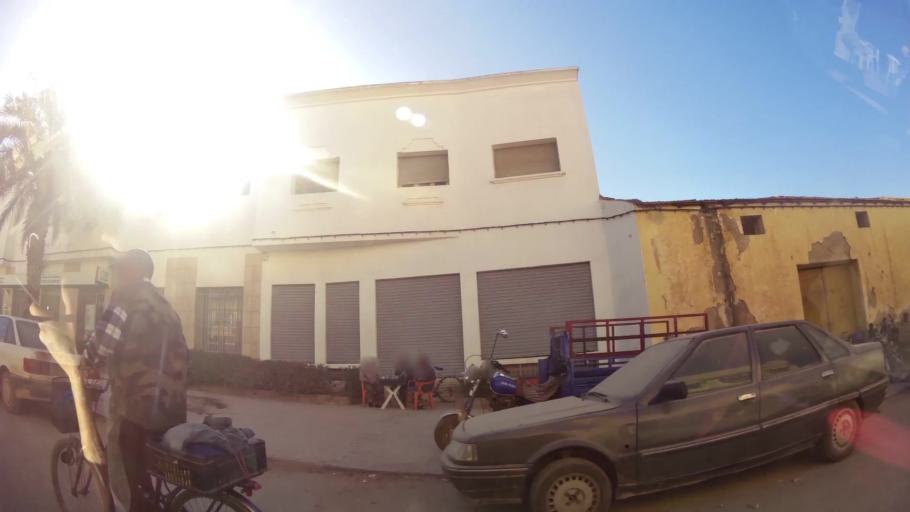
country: MA
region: Oriental
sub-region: Berkane-Taourirt
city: Ahfir
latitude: 34.9505
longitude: -2.1012
